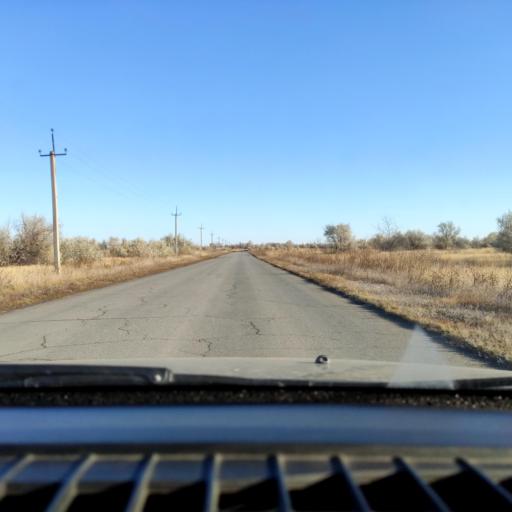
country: RU
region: Samara
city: Tol'yatti
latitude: 53.6530
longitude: 49.3260
